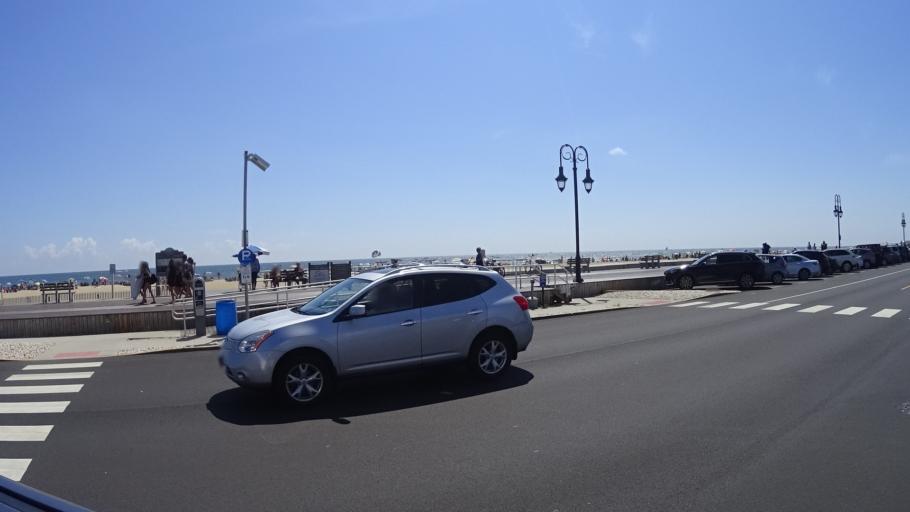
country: US
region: New Jersey
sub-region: Monmouth County
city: Belmar
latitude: 40.1782
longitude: -74.0133
